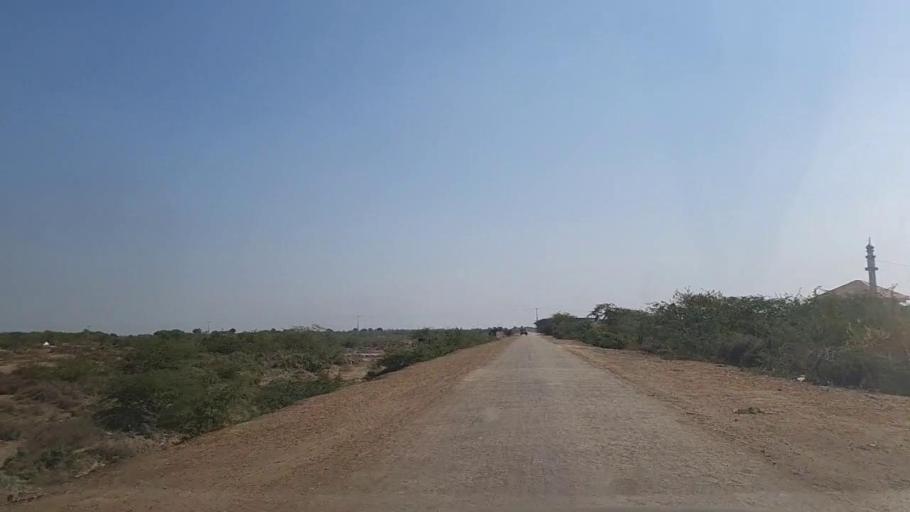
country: PK
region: Sindh
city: Digri
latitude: 25.1681
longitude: 69.1666
